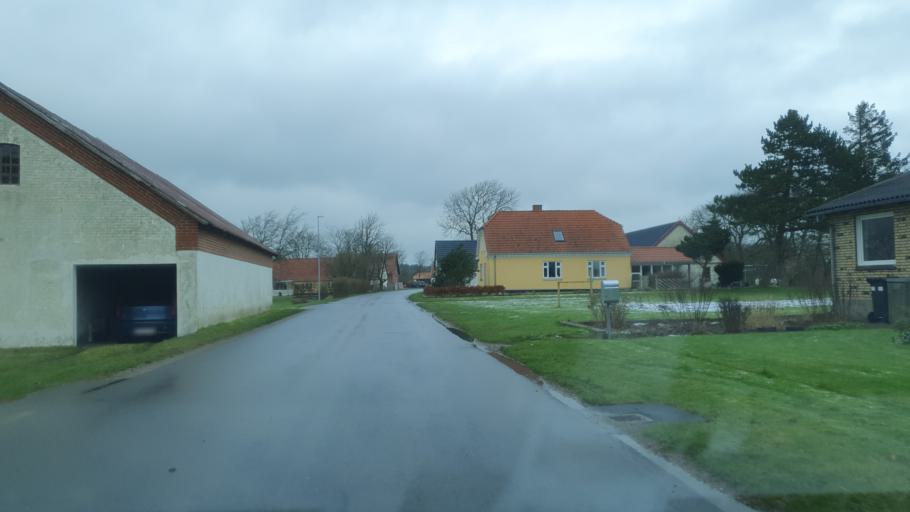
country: DK
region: North Denmark
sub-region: Jammerbugt Kommune
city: Fjerritslev
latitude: 57.1060
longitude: 9.1242
